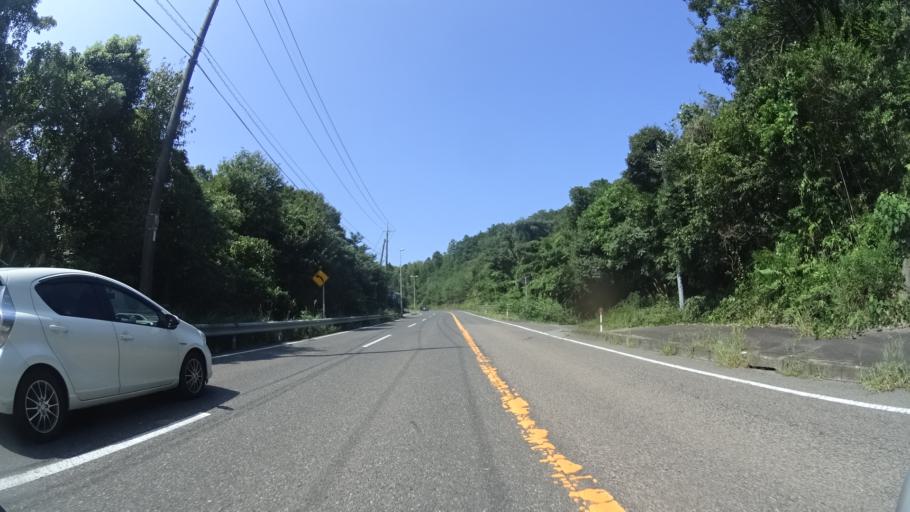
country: JP
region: Shimane
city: Masuda
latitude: 34.6670
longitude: 131.6933
